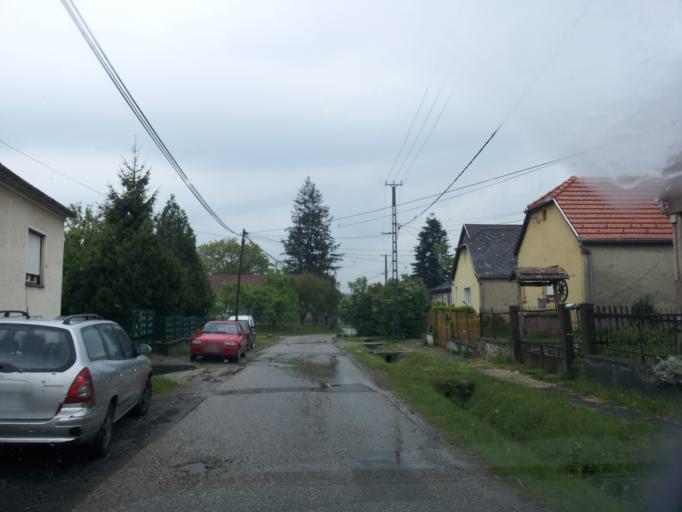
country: HU
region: Baranya
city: Hosszuheteny
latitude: 46.1712
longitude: 18.3489
